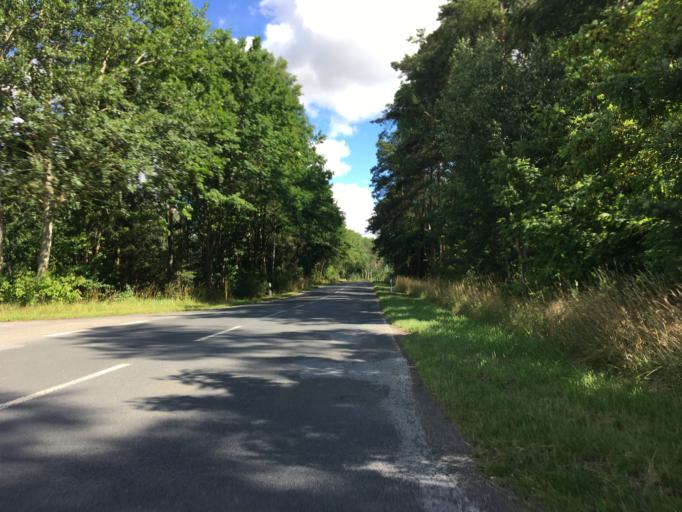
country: DE
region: Brandenburg
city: Mittenwalde
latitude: 53.1911
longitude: 13.5917
